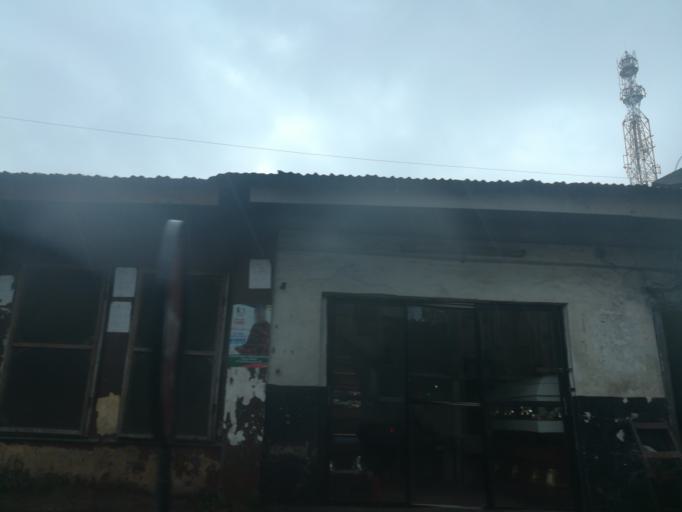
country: NG
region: Lagos
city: Lagos
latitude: 6.4521
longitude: 3.3921
